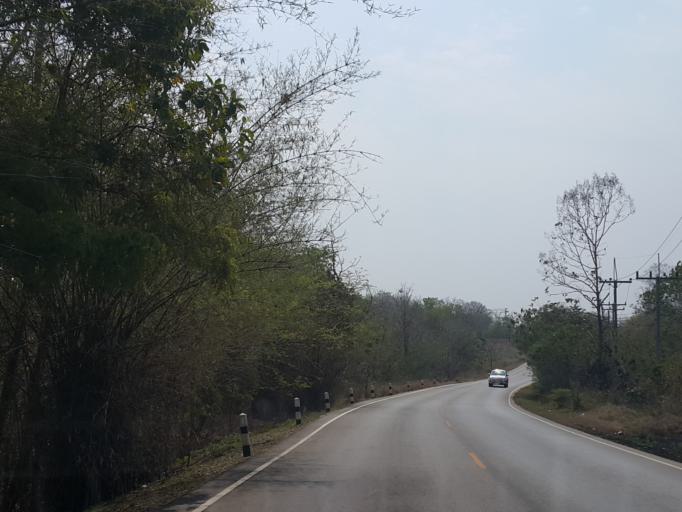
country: TH
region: Lampang
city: Mueang Pan
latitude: 18.7681
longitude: 99.5554
